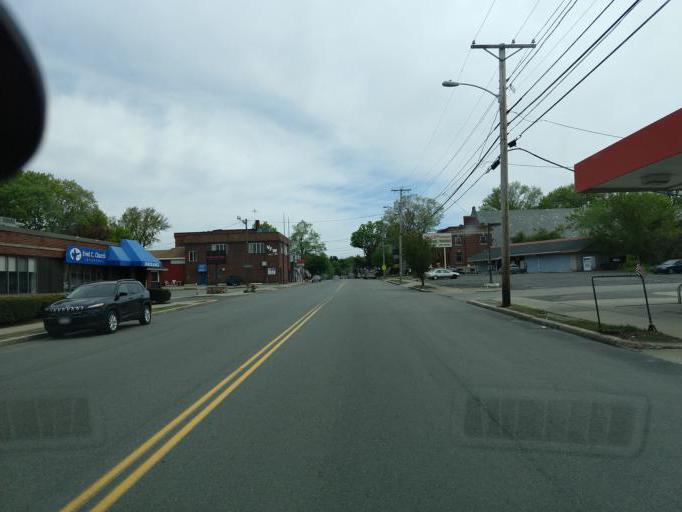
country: US
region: Massachusetts
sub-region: Essex County
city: Haverhill
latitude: 42.7819
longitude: -71.0758
